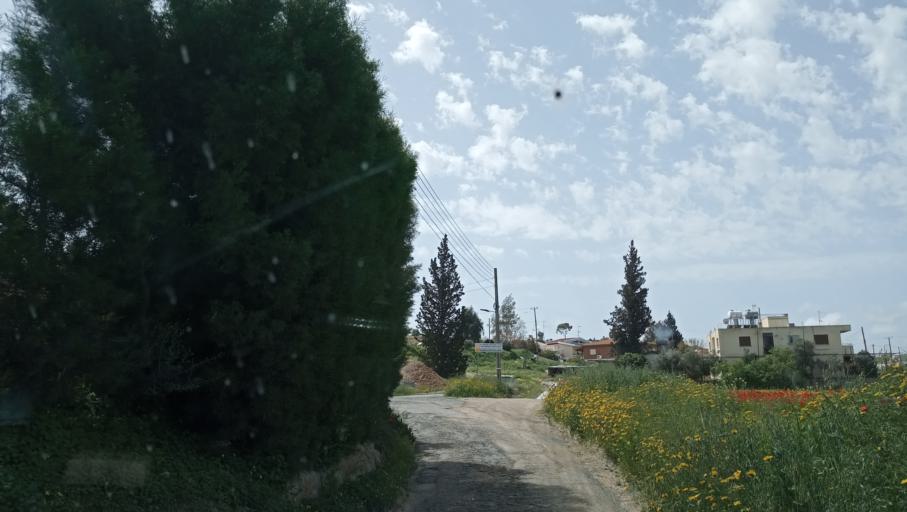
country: CY
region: Lefkosia
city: Dali
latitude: 35.0160
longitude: 33.4183
